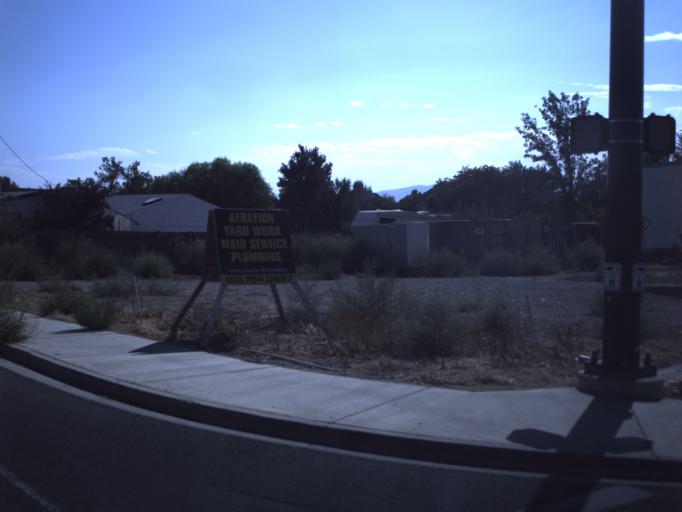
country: US
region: Utah
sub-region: Utah County
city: American Fork
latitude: 40.3830
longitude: -111.7692
